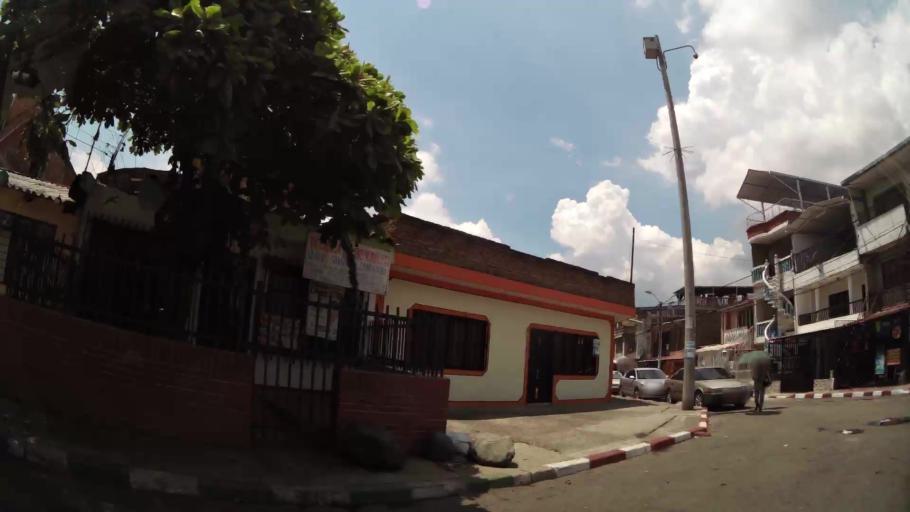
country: CO
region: Valle del Cauca
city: Cali
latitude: 3.4500
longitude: -76.4807
